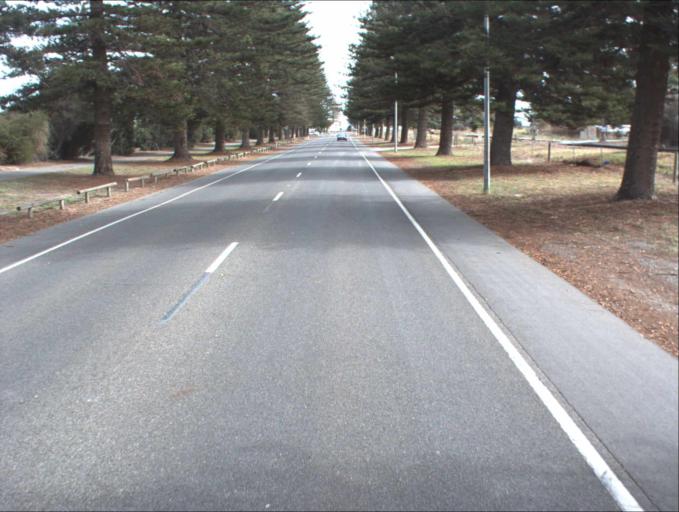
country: AU
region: South Australia
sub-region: Port Adelaide Enfield
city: Birkenhead
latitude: -34.7826
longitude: 138.4874
